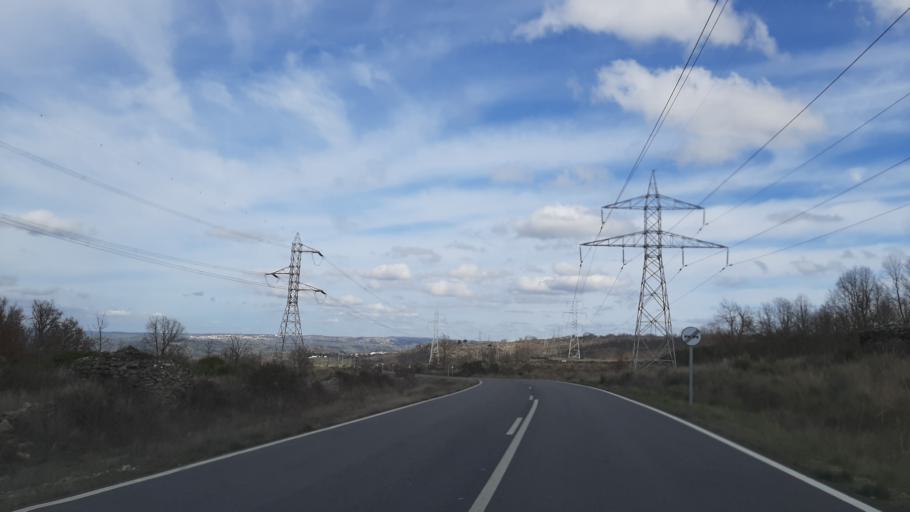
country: ES
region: Castille and Leon
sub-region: Provincia de Salamanca
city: Villarino de los Aires
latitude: 41.2549
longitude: -6.4838
